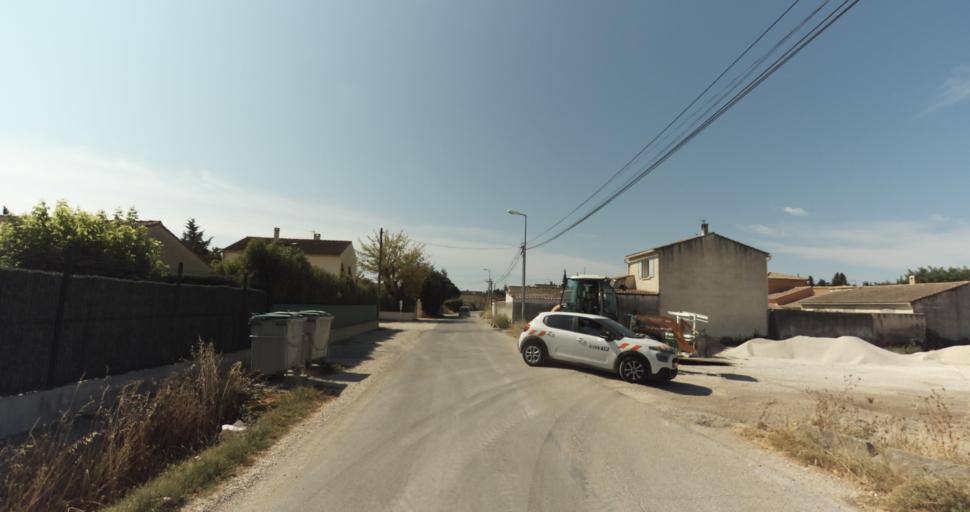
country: FR
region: Provence-Alpes-Cote d'Azur
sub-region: Departement du Vaucluse
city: Monteux
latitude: 44.0246
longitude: 4.9973
